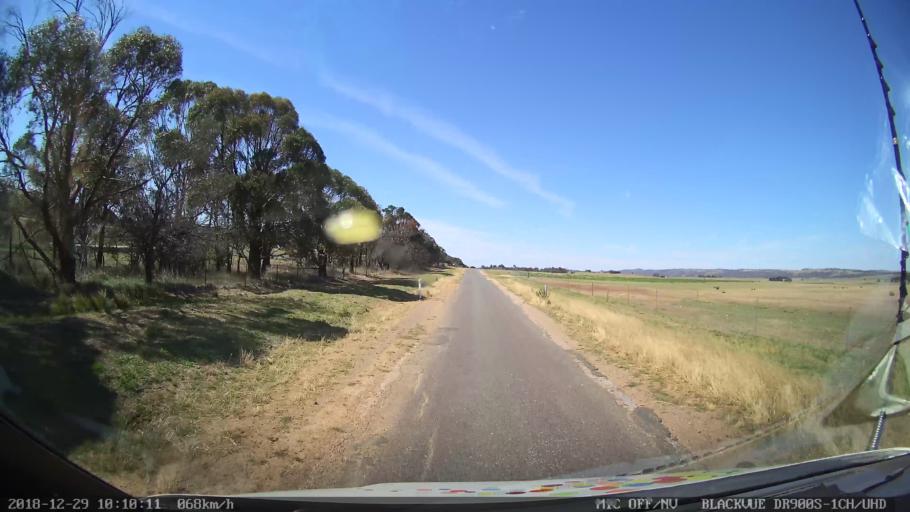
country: AU
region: New South Wales
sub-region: Yass Valley
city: Gundaroo
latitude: -34.8733
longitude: 149.4579
